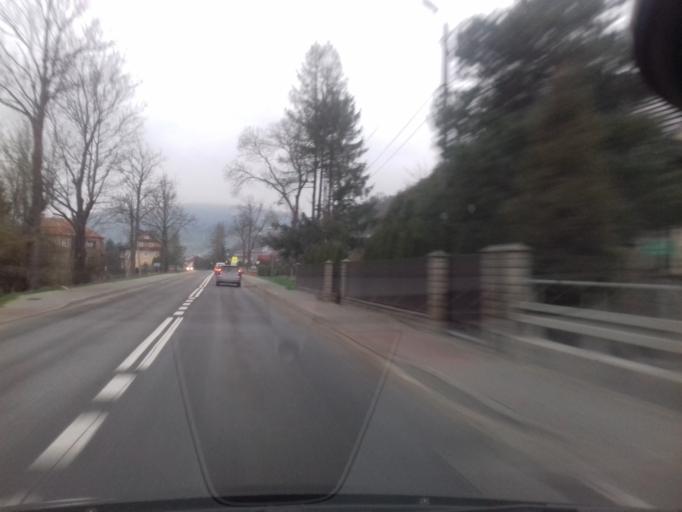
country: PL
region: Lesser Poland Voivodeship
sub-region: Powiat limanowski
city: Mszana Dolna
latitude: 49.6979
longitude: 20.0416
